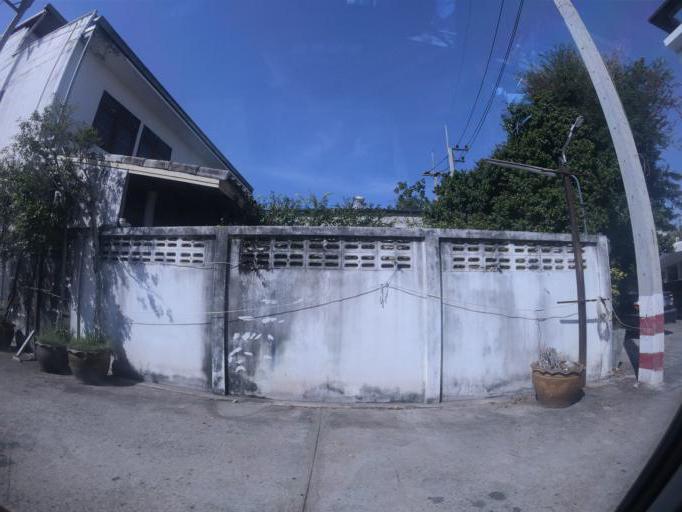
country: TH
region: Maha Sarakham
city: Chiang Yuen
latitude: 16.3732
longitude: 102.9697
